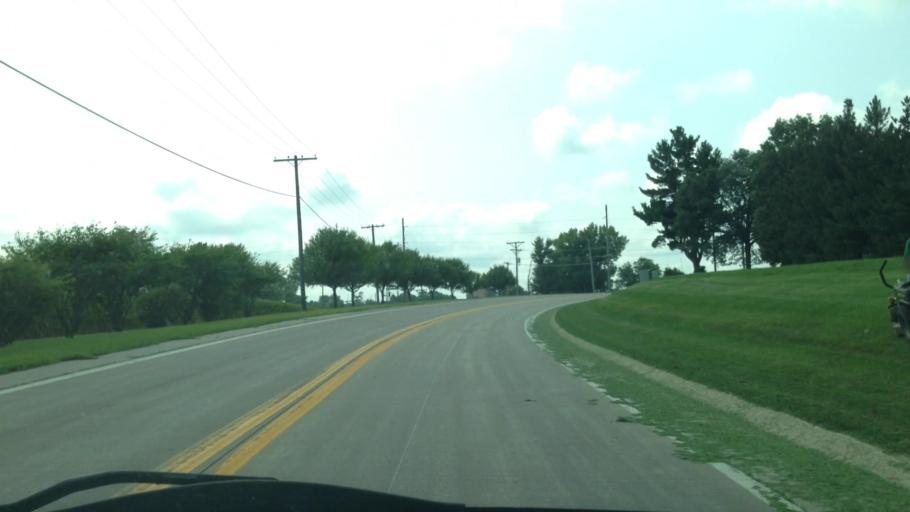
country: US
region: Iowa
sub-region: Linn County
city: Fairfax
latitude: 41.9158
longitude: -91.7837
